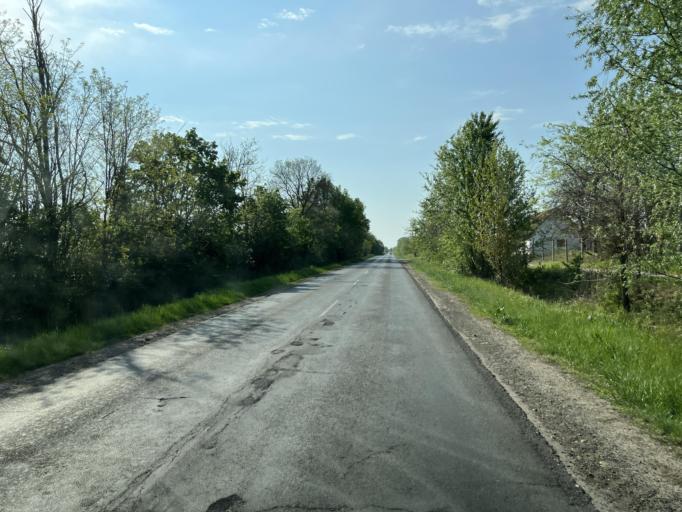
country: HU
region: Pest
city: Jaszkarajeno
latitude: 47.0687
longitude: 20.0510
